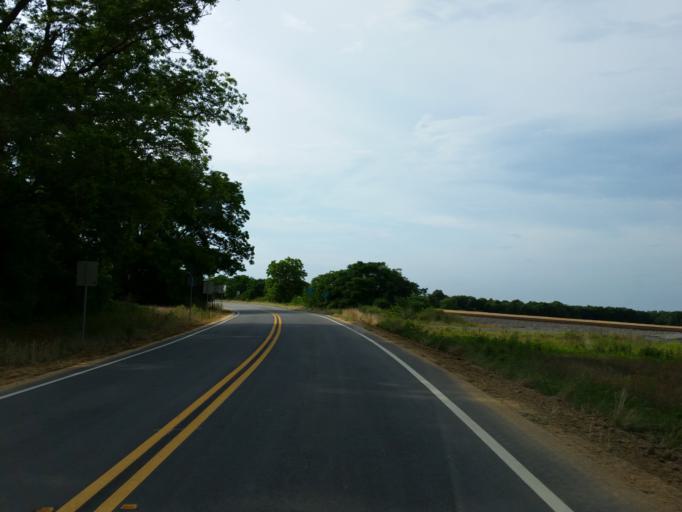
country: US
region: Georgia
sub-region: Turner County
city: Ashburn
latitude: 31.8040
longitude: -83.7124
